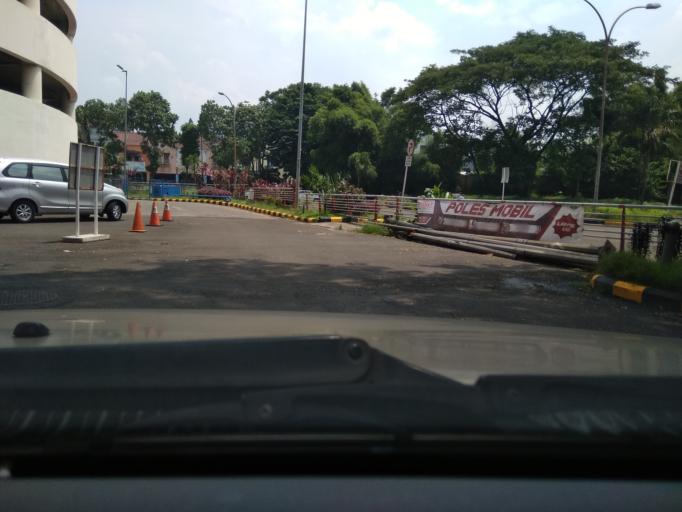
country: ID
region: West Java
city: Serpong
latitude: -6.2854
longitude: 106.6639
